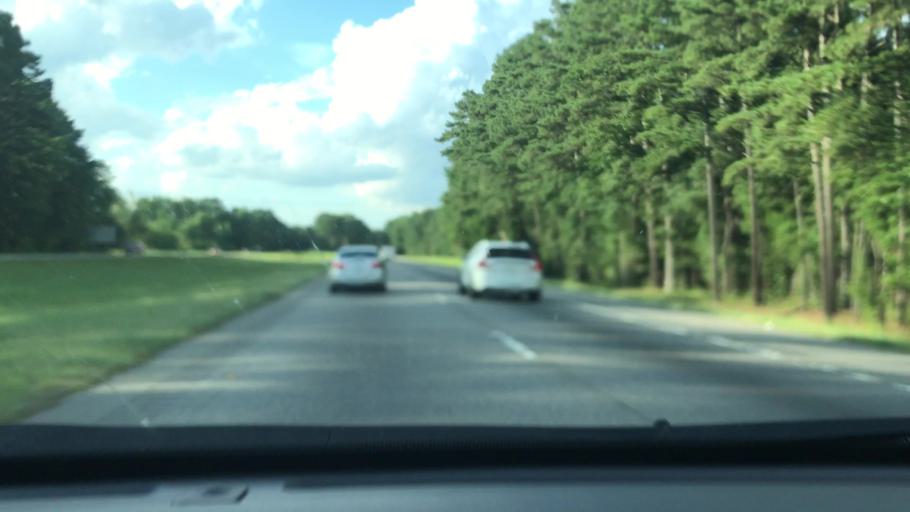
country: US
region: North Carolina
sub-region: Robeson County
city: Saint Pauls
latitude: 34.8218
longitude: -78.9835
